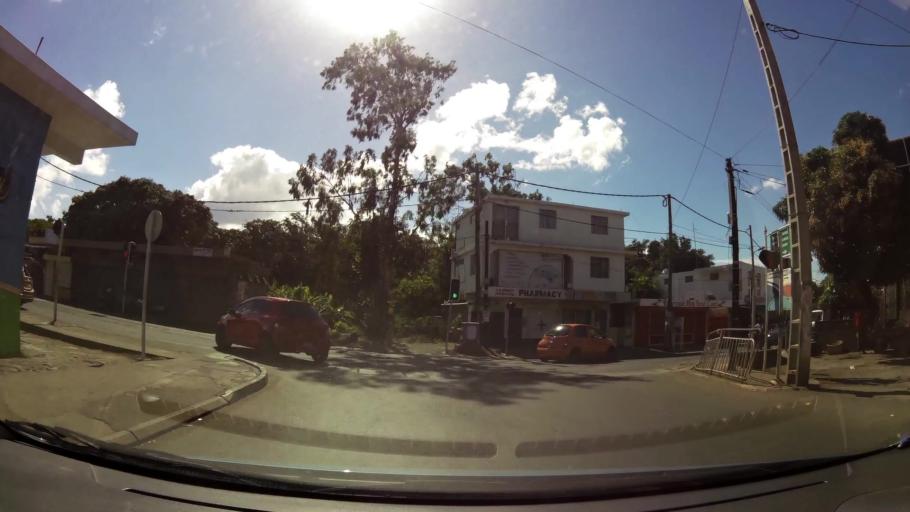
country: MU
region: Black River
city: Cascavelle
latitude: -20.2571
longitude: 57.4178
